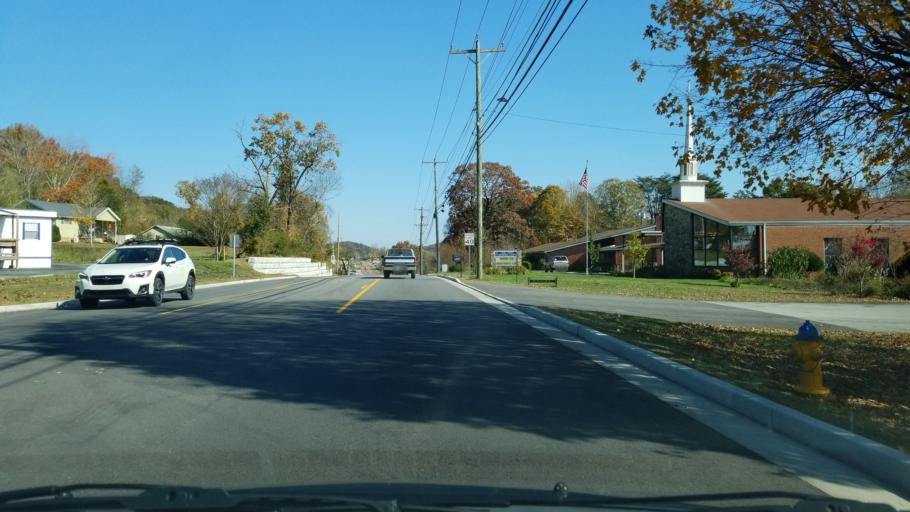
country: US
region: Tennessee
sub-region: Hamilton County
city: Soddy-Daisy
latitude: 35.2388
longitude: -85.1967
